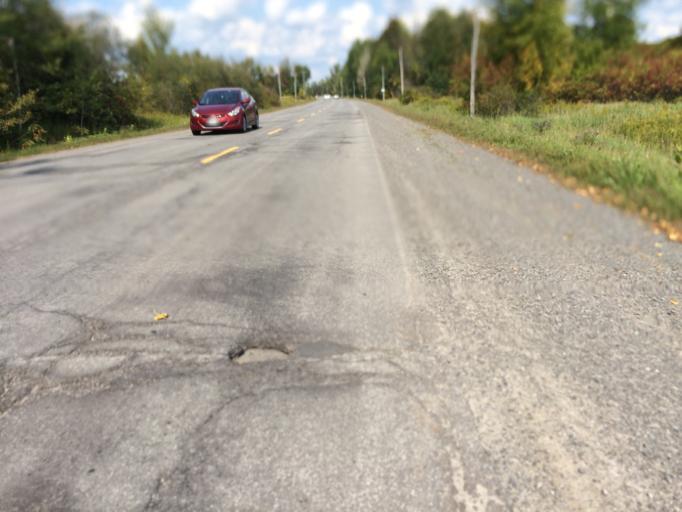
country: CA
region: Ontario
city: Bells Corners
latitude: 45.1779
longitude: -75.6391
